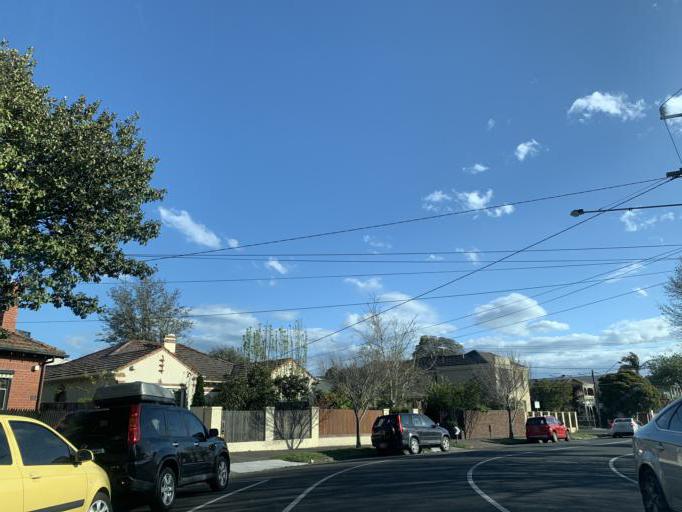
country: AU
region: Victoria
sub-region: Bayside
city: North Brighton
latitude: -37.9062
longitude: 145.0015
